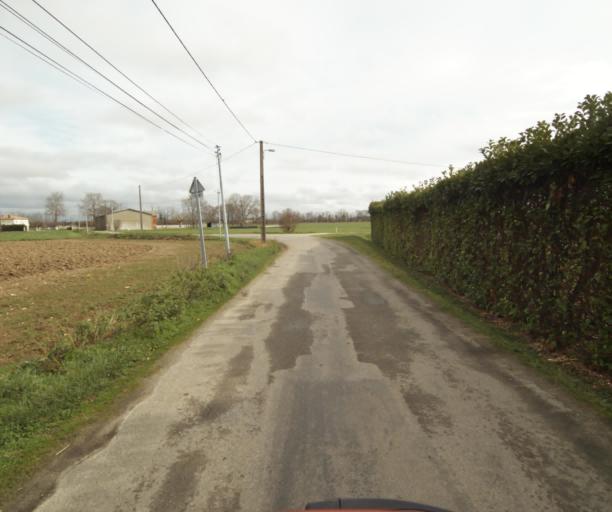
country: FR
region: Midi-Pyrenees
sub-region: Departement de l'Ariege
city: La Tour-du-Crieu
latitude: 43.1240
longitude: 1.6307
